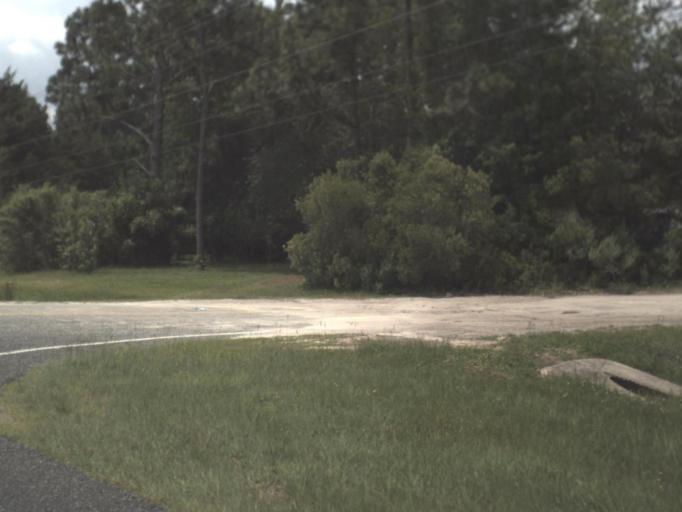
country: US
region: Florida
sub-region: Putnam County
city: East Palatka
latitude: 29.7890
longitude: -81.6479
